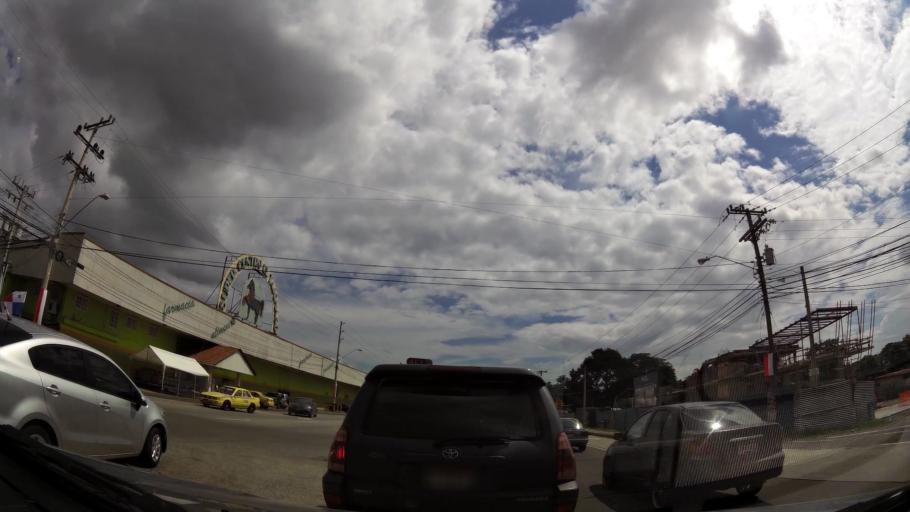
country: PA
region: Panama
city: Nuevo Arraijan
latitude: 8.9256
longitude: -79.7139
